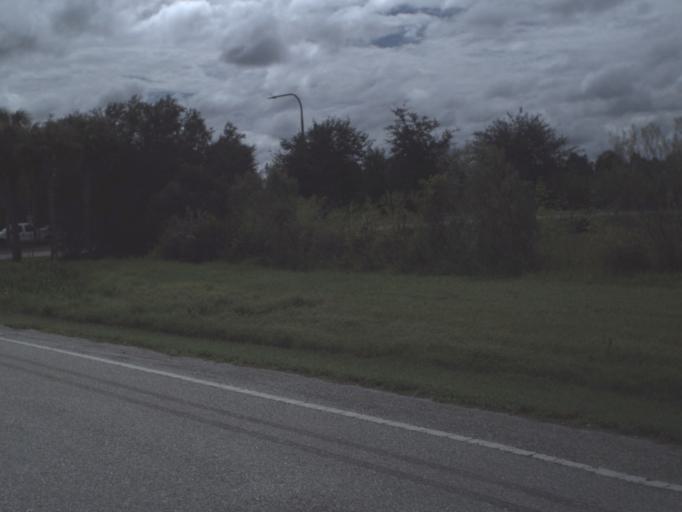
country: US
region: Florida
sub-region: Sarasota County
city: Plantation
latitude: 27.0800
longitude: -82.3311
